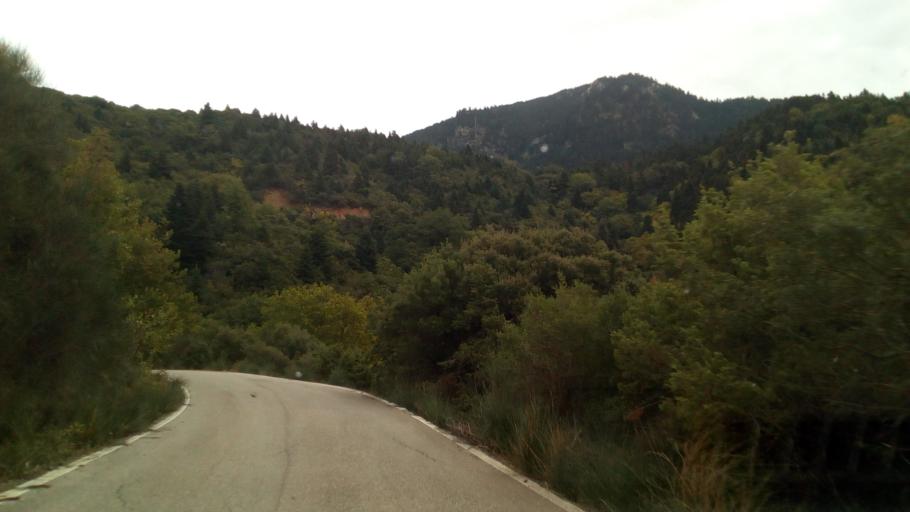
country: GR
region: West Greece
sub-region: Nomos Aitolias kai Akarnanias
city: Thermo
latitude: 38.5861
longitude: 21.8480
